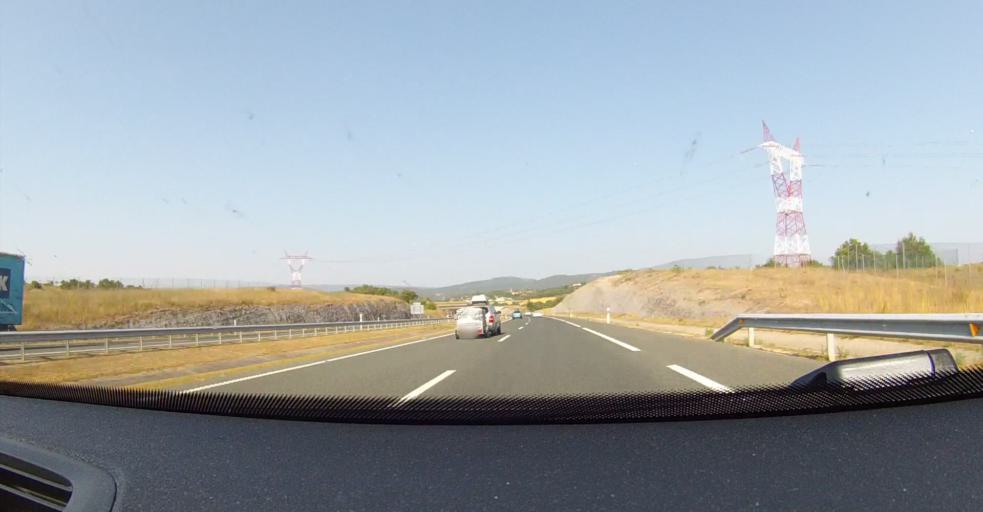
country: ES
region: Basque Country
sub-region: Provincia de Alava
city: Gasteiz / Vitoria
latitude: 42.9179
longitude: -2.6864
